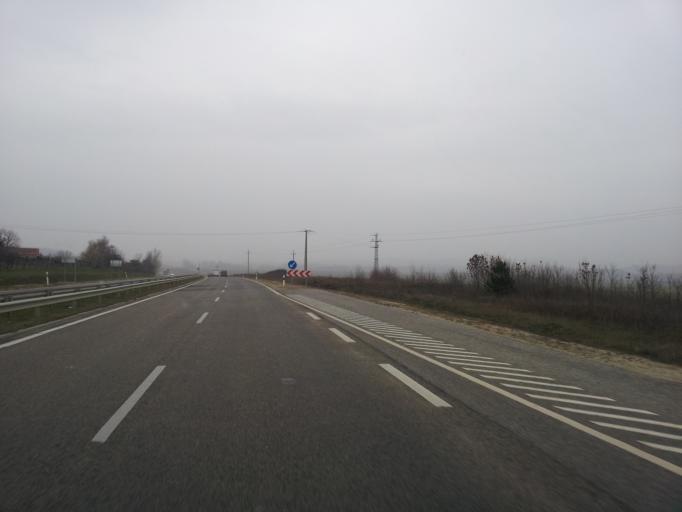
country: HU
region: Veszprem
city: Herend
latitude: 47.1223
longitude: 17.7954
